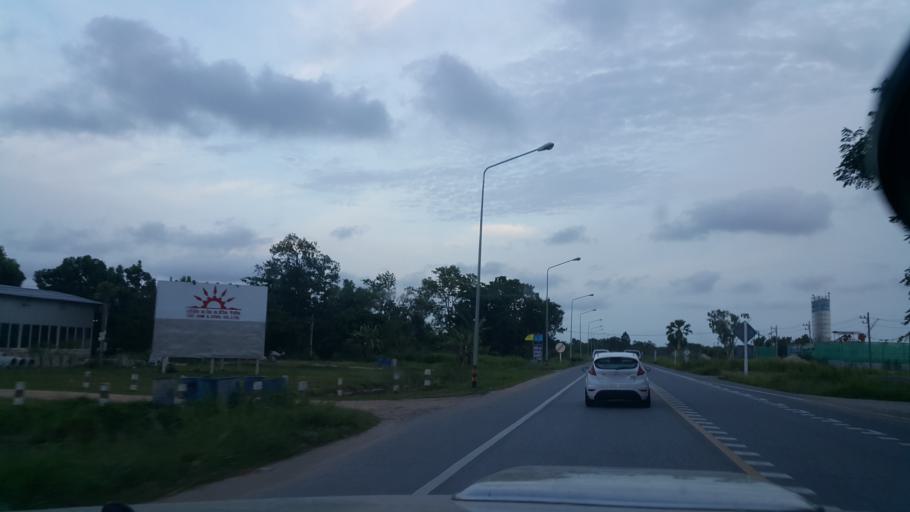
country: TH
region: Rayong
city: Ban Chang
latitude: 12.7125
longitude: 101.0032
